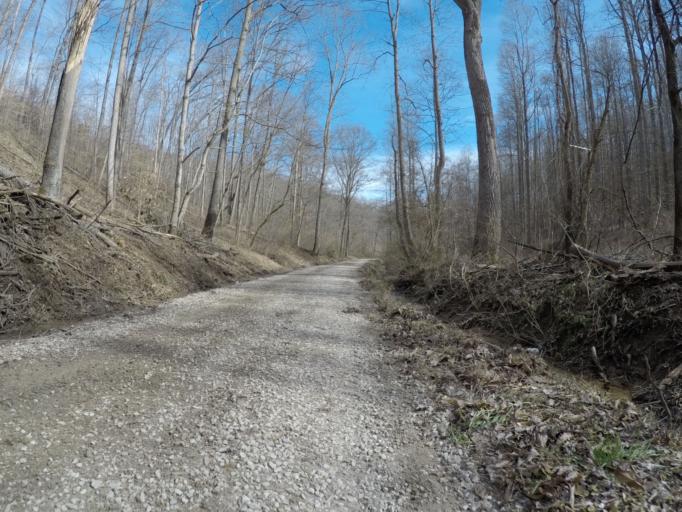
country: US
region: West Virginia
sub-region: Wayne County
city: Ceredo
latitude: 38.3443
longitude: -82.5440
